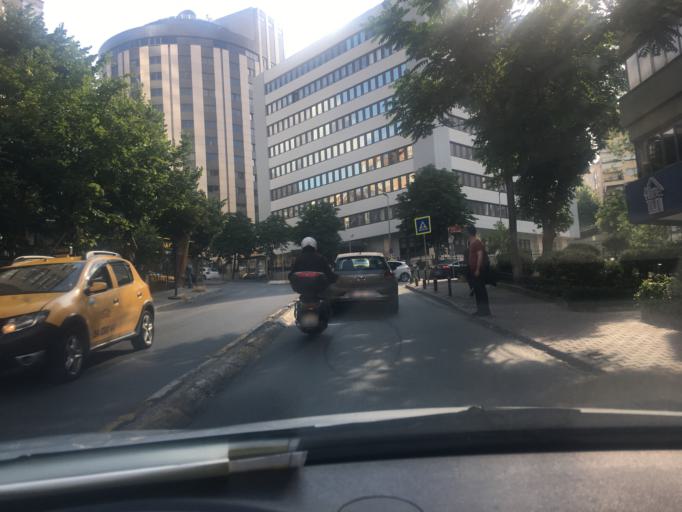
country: TR
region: Istanbul
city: Sisli
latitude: 41.0643
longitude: 29.0020
